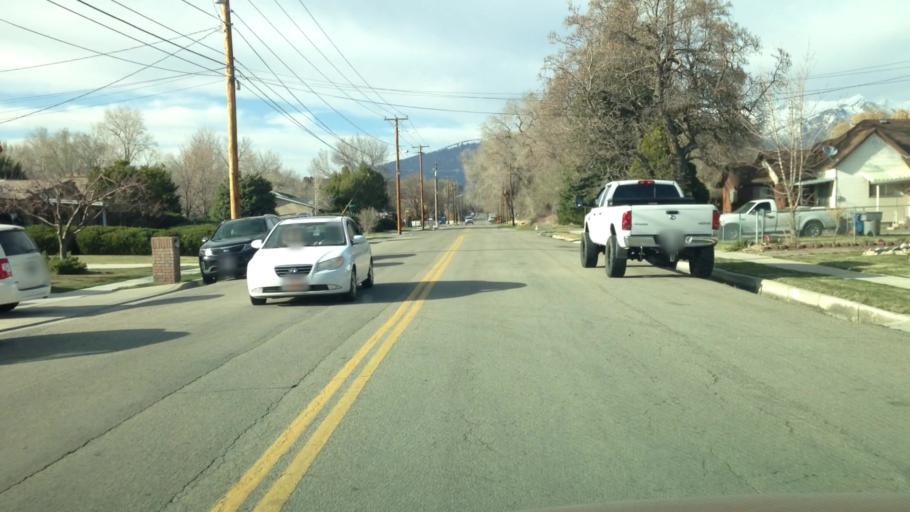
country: US
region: Utah
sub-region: Utah County
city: American Fork
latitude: 40.3862
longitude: -111.7932
